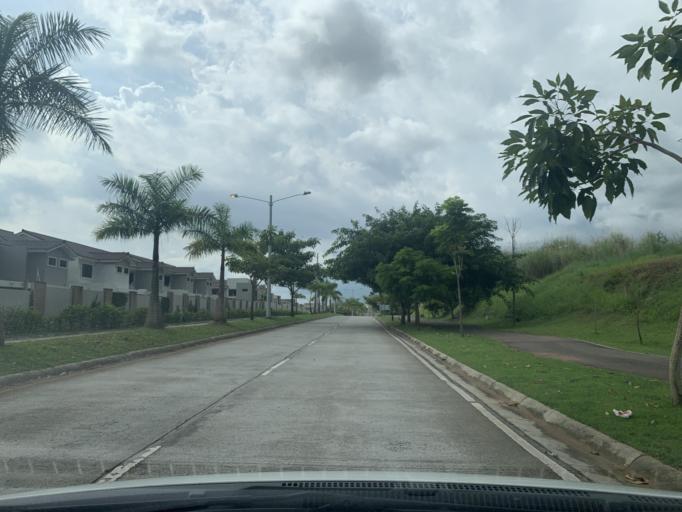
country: PA
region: Panama
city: San Miguelito
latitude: 9.0891
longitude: -79.4654
